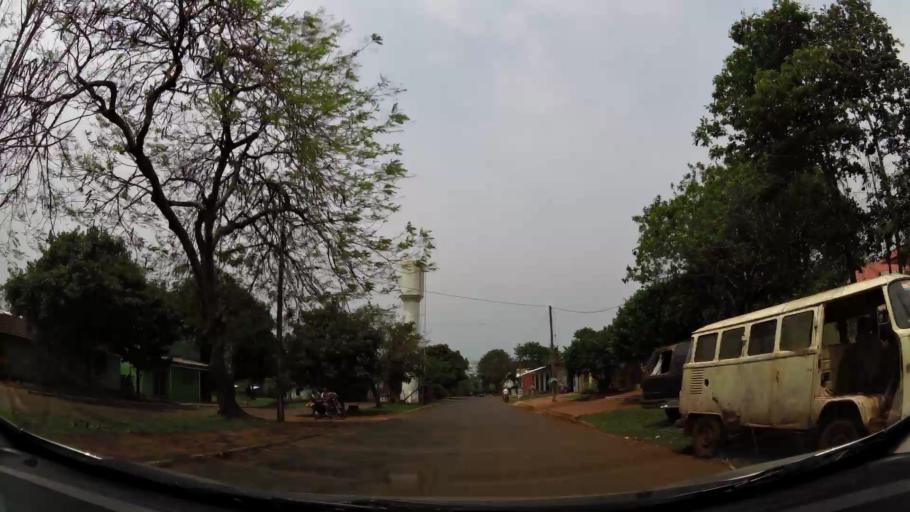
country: PY
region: Alto Parana
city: Presidente Franco
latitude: -25.5577
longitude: -54.6148
